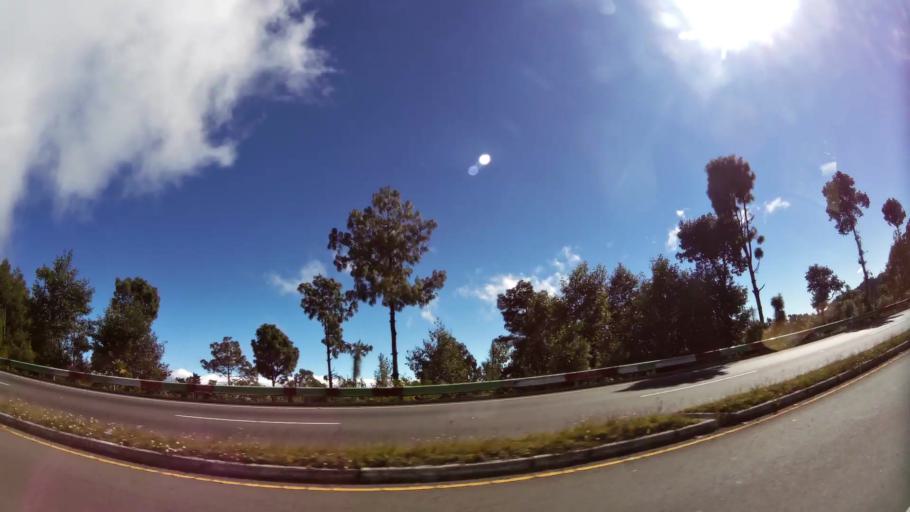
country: GT
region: Solola
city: Santa Catarina Ixtahuacan
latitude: 14.8317
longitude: -91.3624
